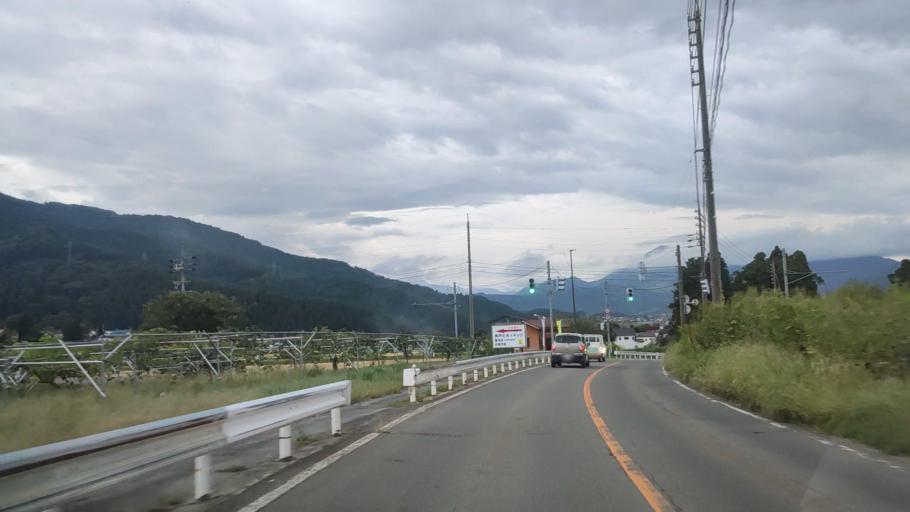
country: JP
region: Nagano
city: Iiyama
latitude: 36.8835
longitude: 138.4123
